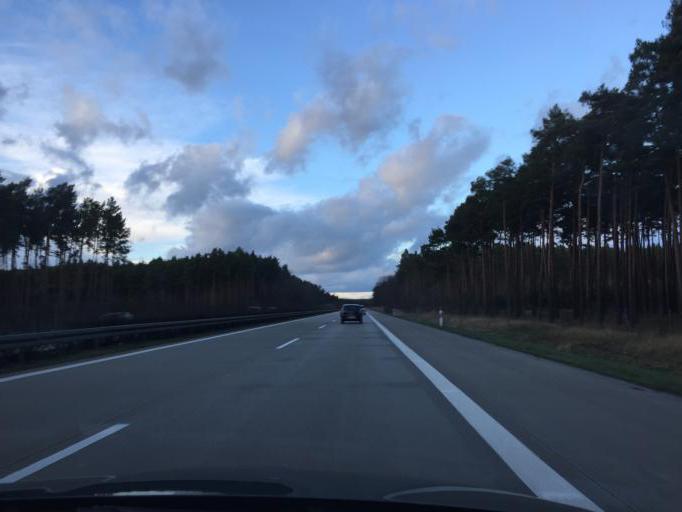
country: DE
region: Brandenburg
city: Schwerin
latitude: 52.1793
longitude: 13.6226
